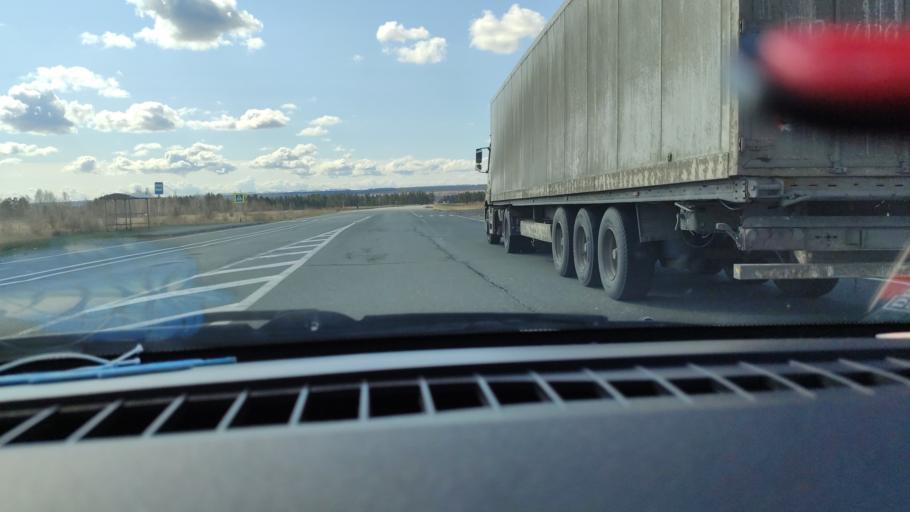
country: RU
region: Samara
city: Varlamovo
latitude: 53.1520
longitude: 48.2843
